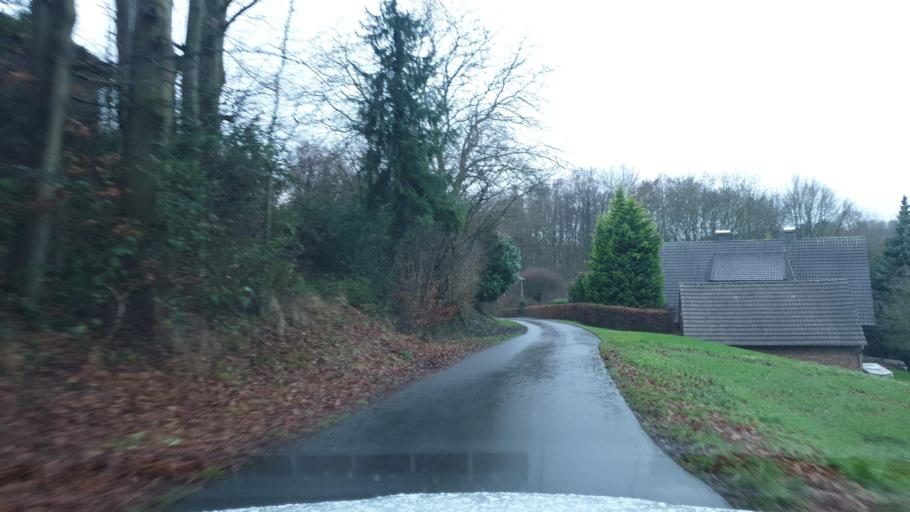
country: DE
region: North Rhine-Westphalia
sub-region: Regierungsbezirk Detmold
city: Hille
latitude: 52.2700
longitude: 8.7573
